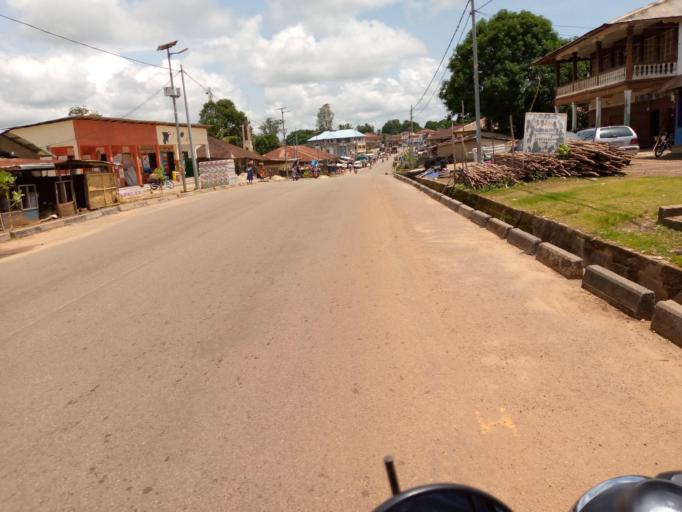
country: SL
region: Northern Province
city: Magburaka
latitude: 8.7223
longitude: -11.9463
